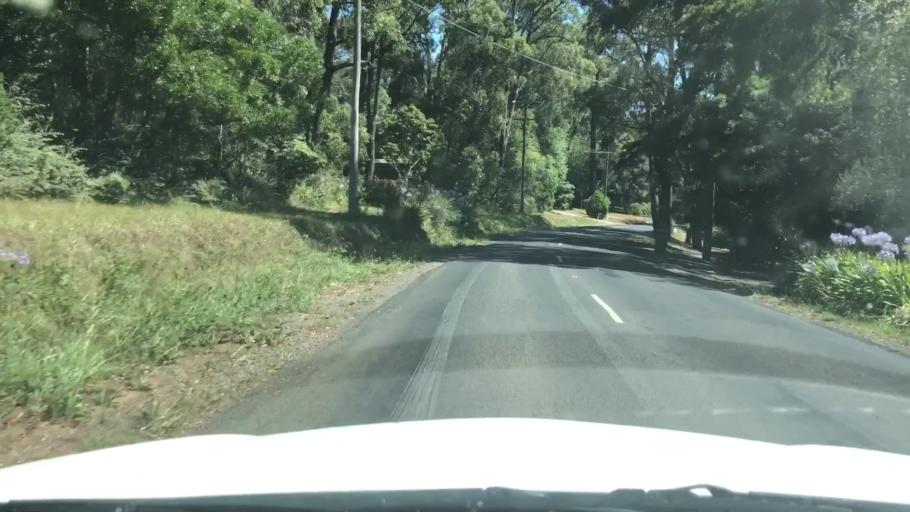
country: AU
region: Victoria
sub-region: Cardinia
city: Cockatoo
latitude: -37.9193
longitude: 145.4692
